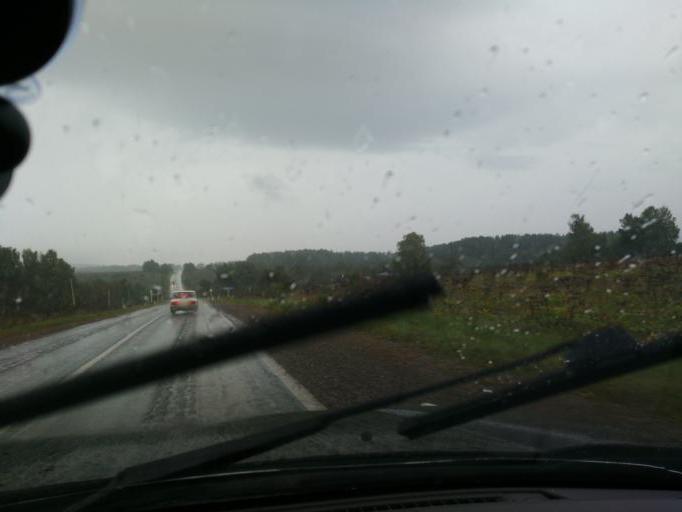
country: RU
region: Perm
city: Osa
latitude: 57.1447
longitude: 55.5289
